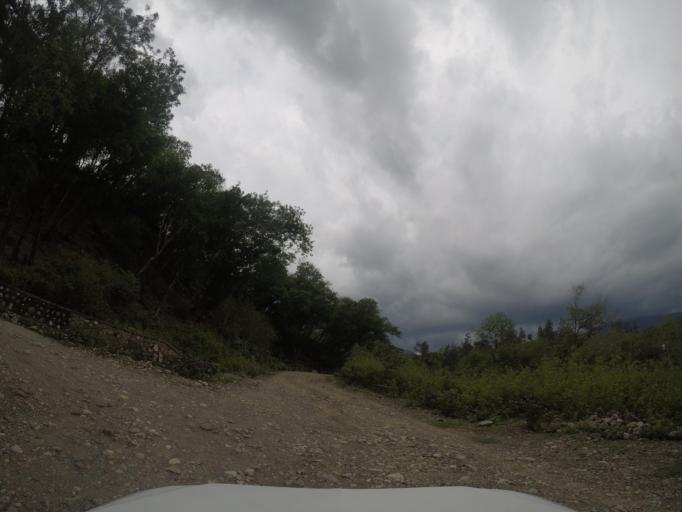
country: TL
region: Bobonaro
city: Maliana
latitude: -8.9737
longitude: 125.2300
